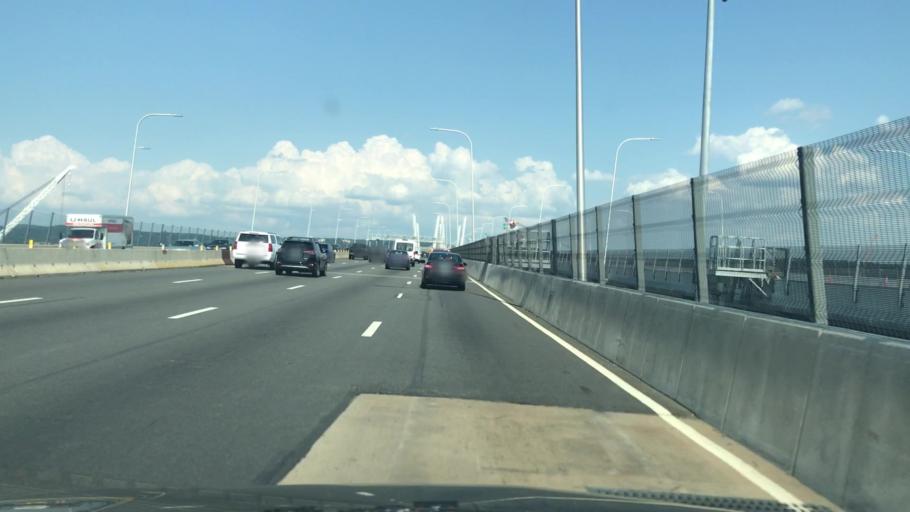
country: US
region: New York
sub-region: Rockland County
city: South Nyack
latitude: 41.0716
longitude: -73.9043
